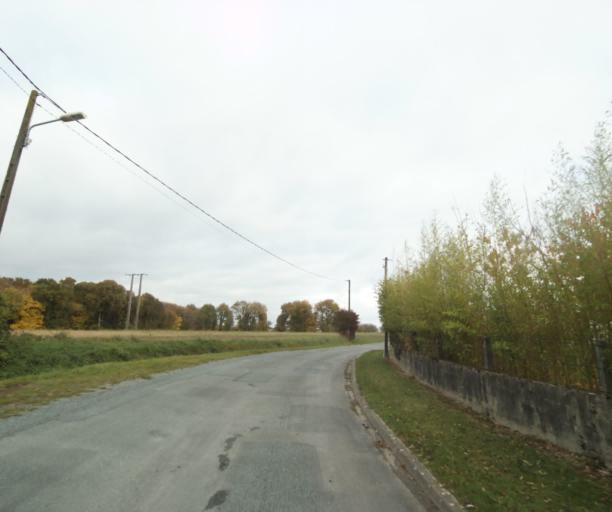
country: FR
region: Poitou-Charentes
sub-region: Departement de la Charente-Maritime
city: Saint-Georges-des-Coteaux
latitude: 45.7707
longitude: -0.7094
